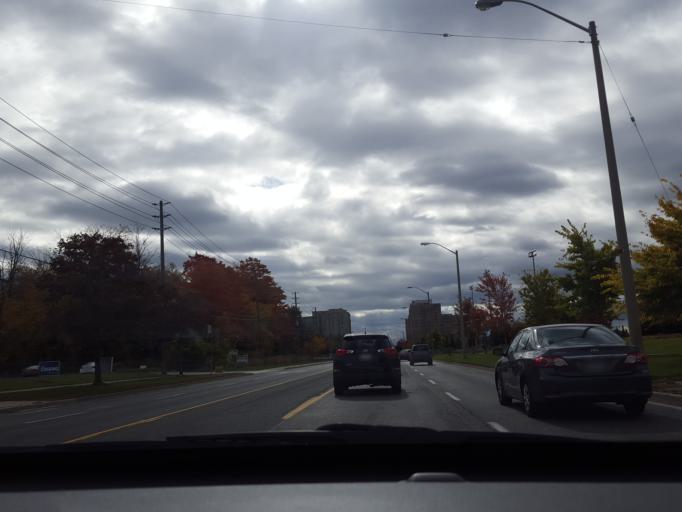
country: CA
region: Ontario
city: Markham
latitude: 43.8171
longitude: -79.3041
